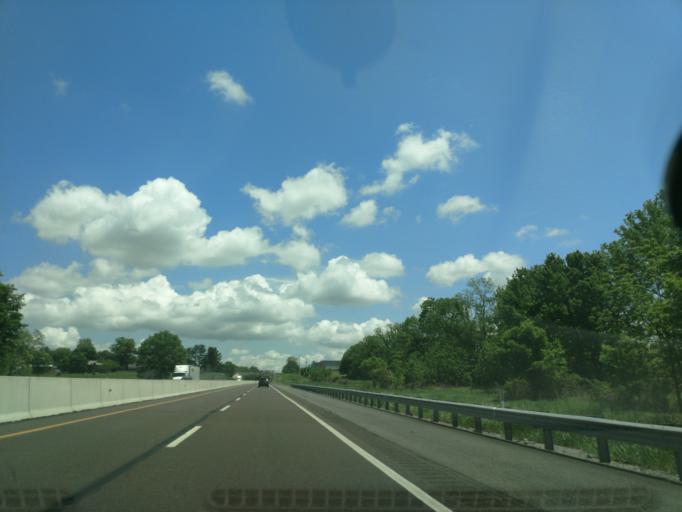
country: US
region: Pennsylvania
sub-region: Lancaster County
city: Schoeneck
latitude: 40.2455
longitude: -76.1820
